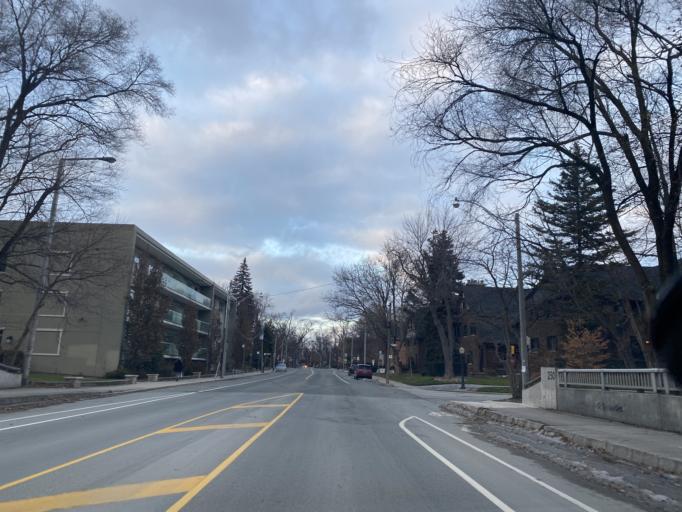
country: CA
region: Ontario
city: Toronto
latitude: 43.6735
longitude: -79.3773
